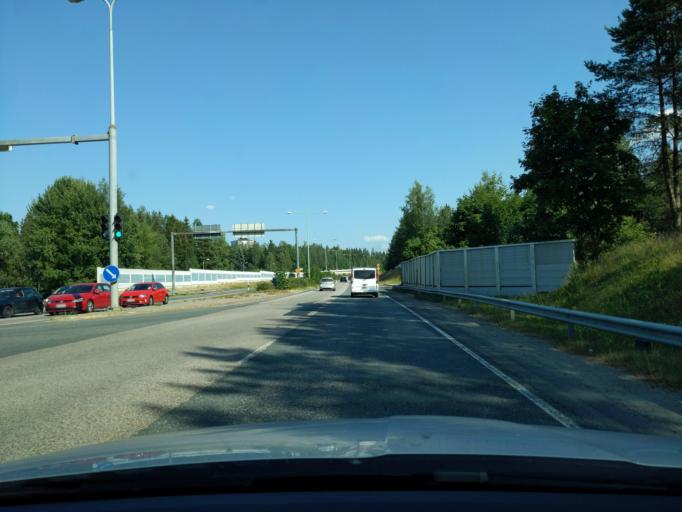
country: FI
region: Paijanne Tavastia
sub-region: Lahti
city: Hollola
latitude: 60.9851
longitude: 25.5791
